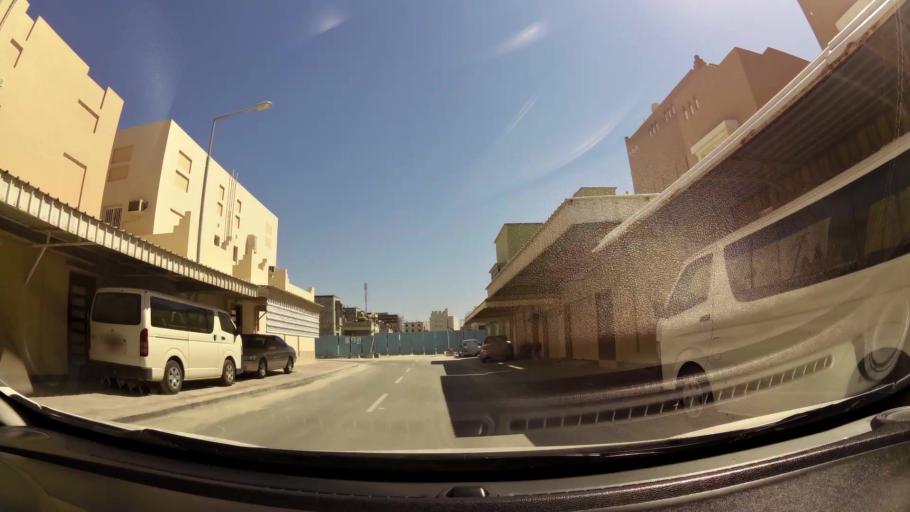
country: BH
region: Muharraq
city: Al Muharraq
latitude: 26.2735
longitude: 50.5969
